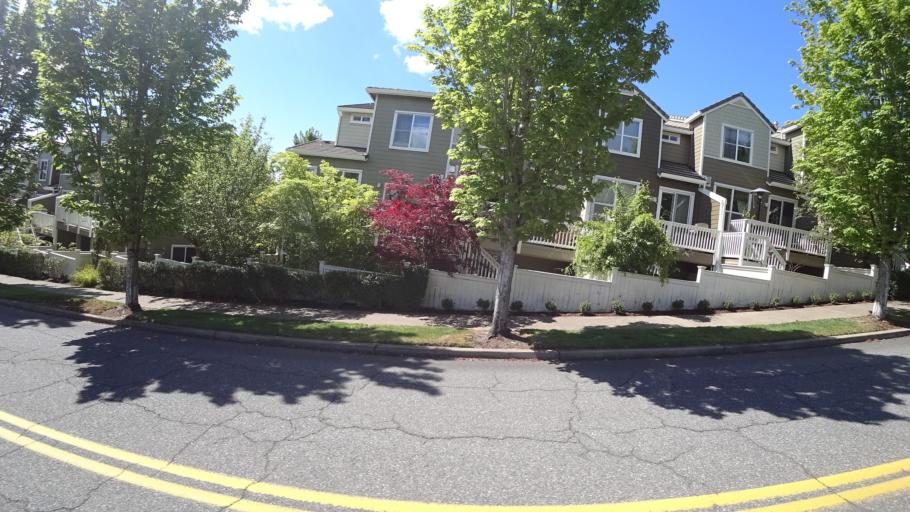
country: US
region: Oregon
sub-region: Washington County
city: West Haven
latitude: 45.5436
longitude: -122.7772
